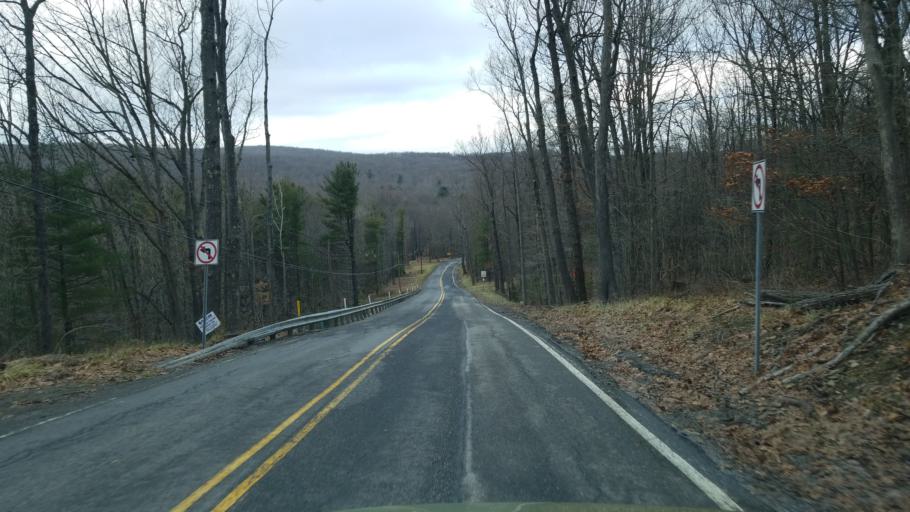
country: US
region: Pennsylvania
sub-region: Clearfield County
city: Hyde
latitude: 41.0500
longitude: -78.4892
